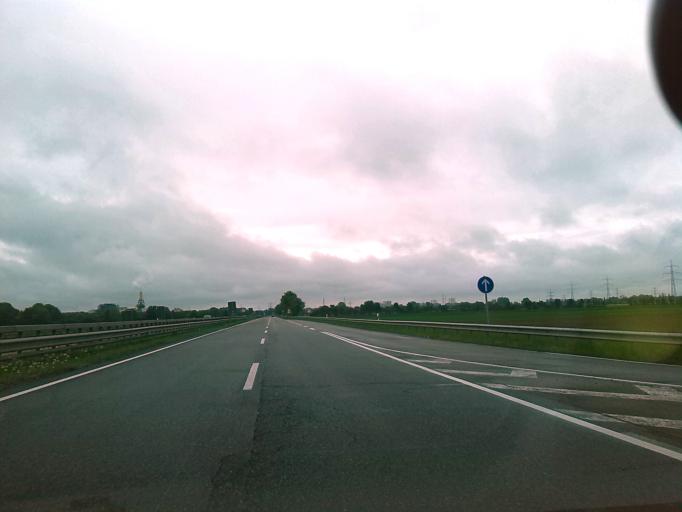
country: DE
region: Rheinland-Pfalz
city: Bobenheim-Roxheim
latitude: 49.5662
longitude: 8.3974
